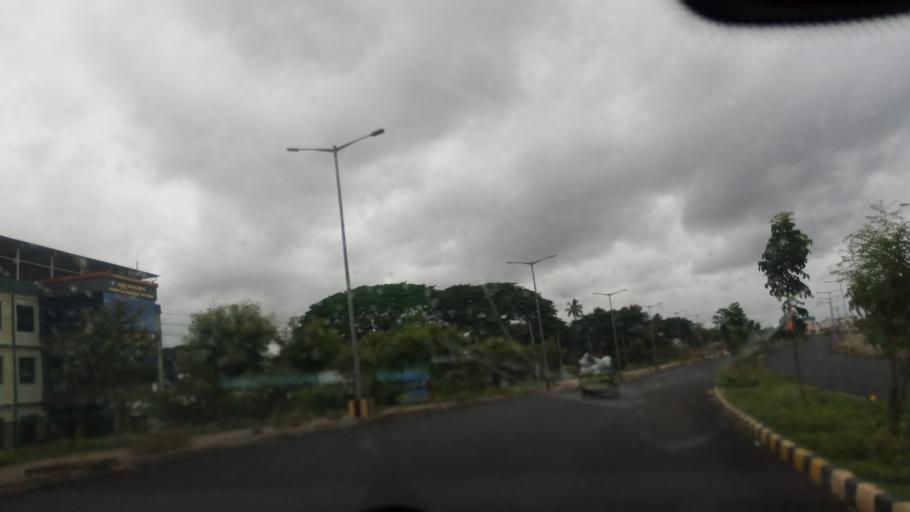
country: IN
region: Karnataka
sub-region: Mysore
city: Mysore
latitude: 12.2854
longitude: 76.6089
